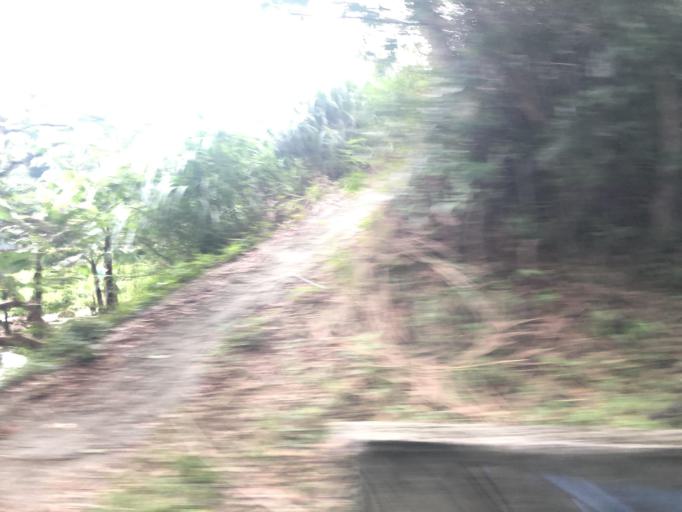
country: TW
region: Taiwan
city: Daxi
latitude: 24.9162
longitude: 121.3501
